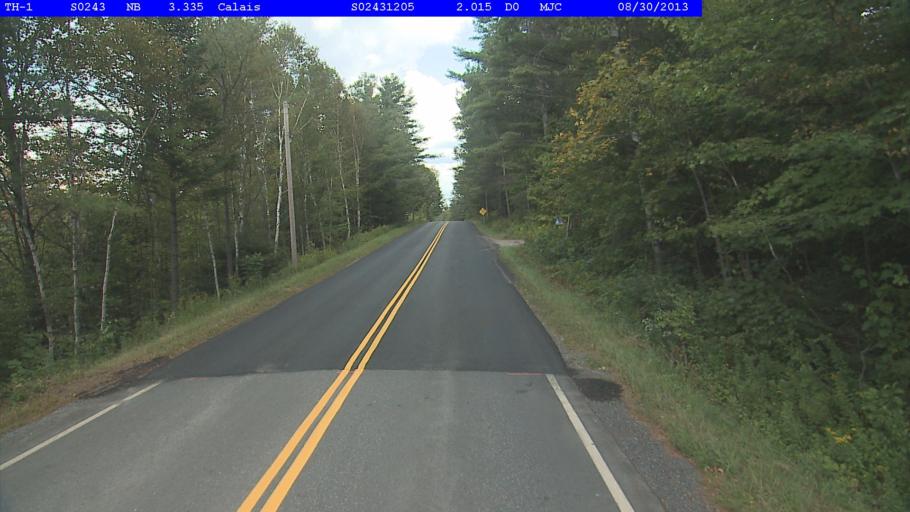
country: US
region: Vermont
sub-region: Washington County
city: Montpelier
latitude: 44.3611
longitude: -72.5065
